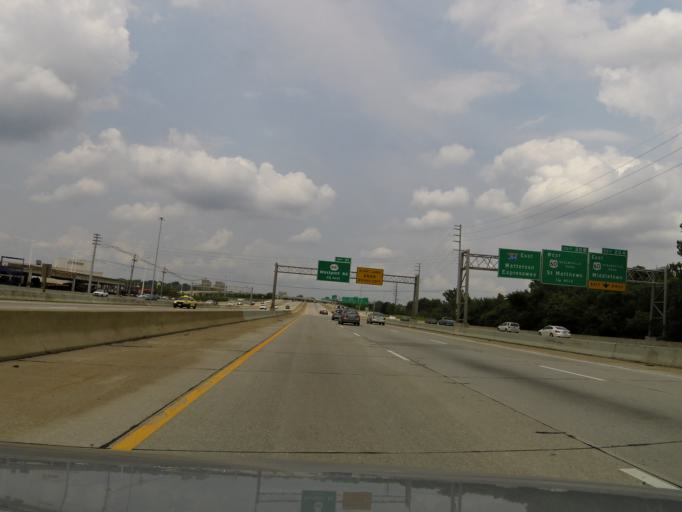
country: US
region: Kentucky
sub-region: Jefferson County
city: Beechwood Village
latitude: 38.2439
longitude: -85.6213
